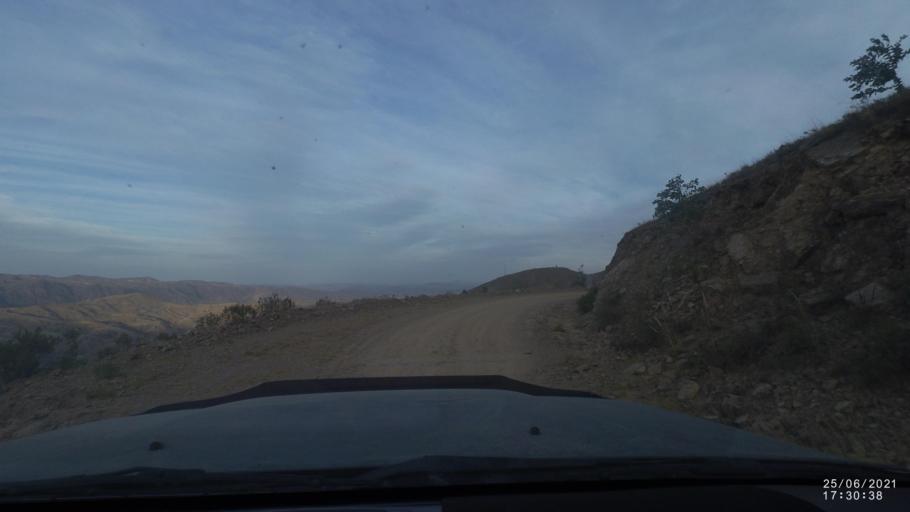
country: BO
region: Cochabamba
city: Mizque
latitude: -17.9346
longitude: -65.6656
